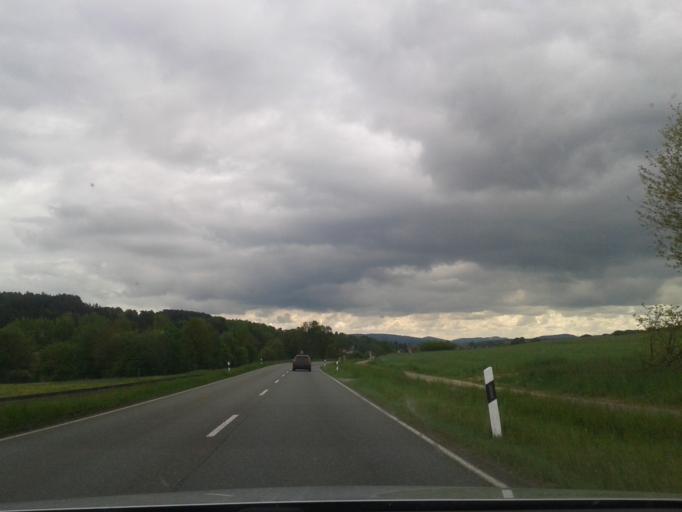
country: DE
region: Hesse
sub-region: Regierungsbezirk Giessen
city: Munchhausen
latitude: 50.9756
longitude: 8.7271
